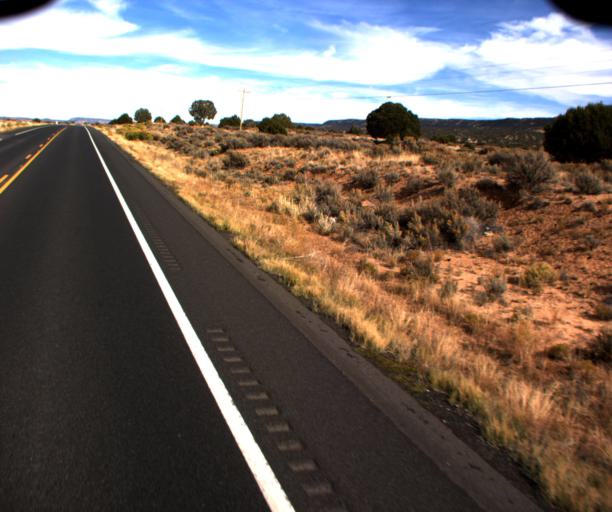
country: US
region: Arizona
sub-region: Navajo County
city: Kayenta
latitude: 36.5004
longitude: -110.6179
